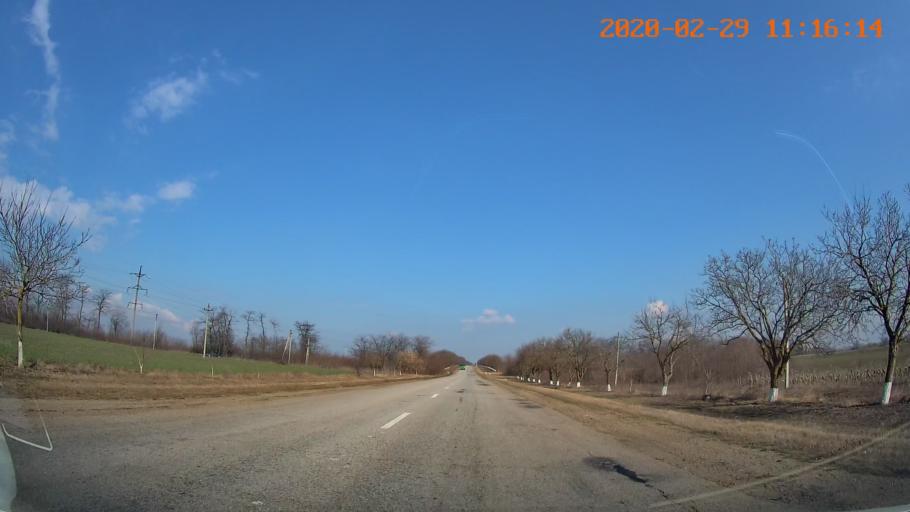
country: MD
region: Telenesti
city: Dubasari
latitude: 47.3059
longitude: 29.1673
